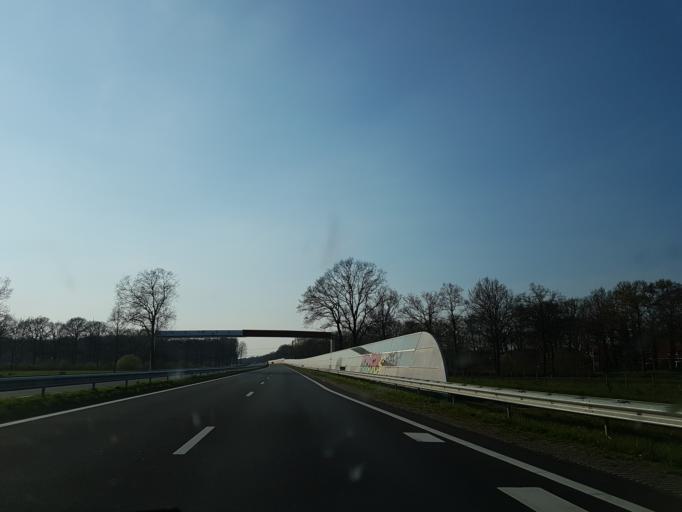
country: NL
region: Overijssel
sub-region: Gemeente Raalte
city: Heino
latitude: 52.4859
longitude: 6.1706
